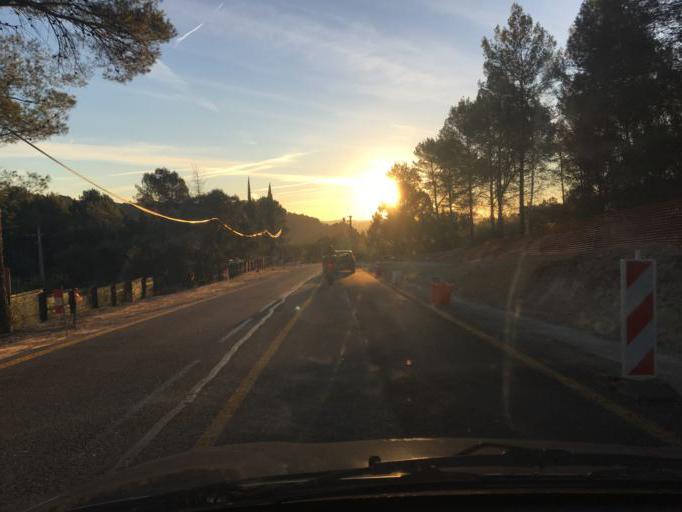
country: FR
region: Provence-Alpes-Cote d'Azur
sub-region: Departement du Var
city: Taradeau
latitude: 43.4607
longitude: 6.4152
